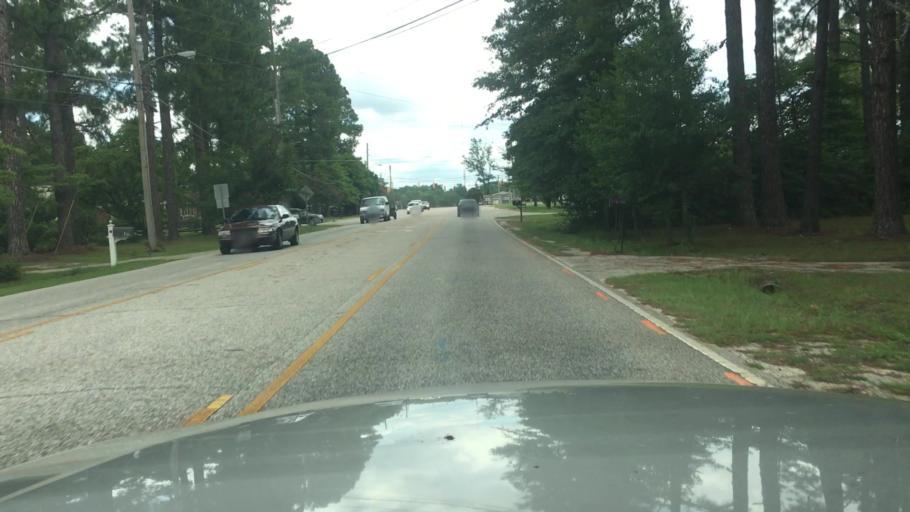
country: US
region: North Carolina
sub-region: Cumberland County
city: Hope Mills
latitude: 35.0414
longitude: -78.9853
